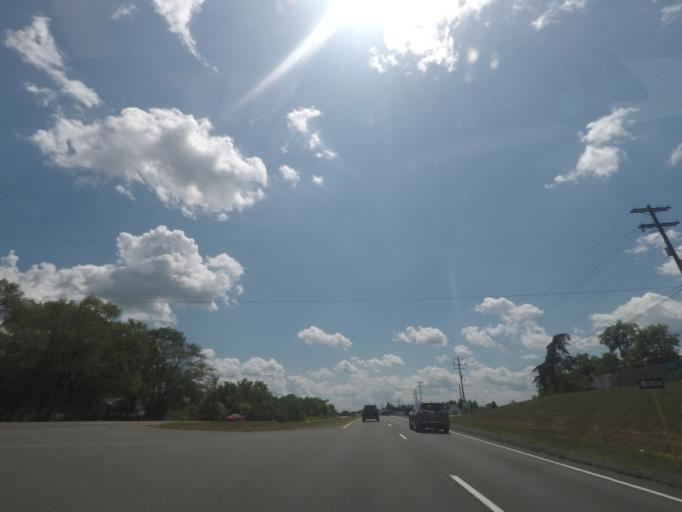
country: US
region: Virginia
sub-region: City of Winchester
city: Winchester
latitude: 39.1477
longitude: -78.1295
